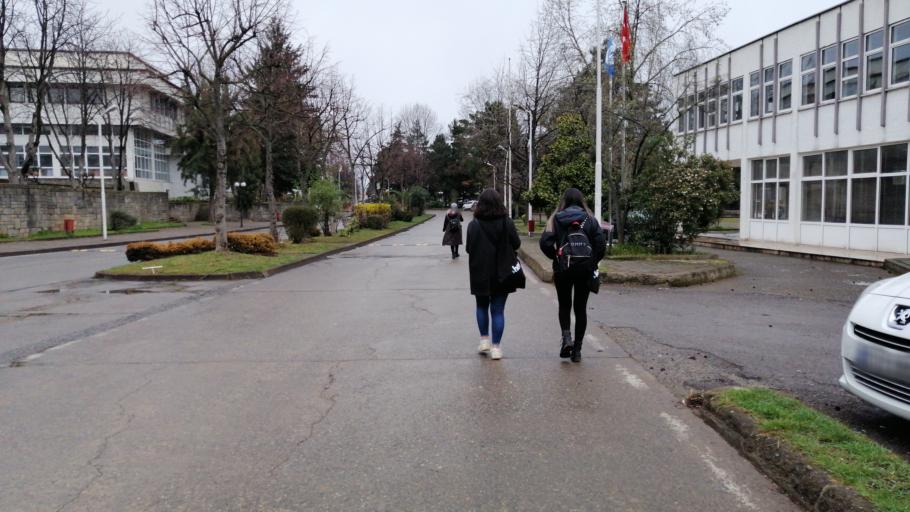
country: TR
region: Trabzon
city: Trabzon
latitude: 40.9937
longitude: 39.7757
